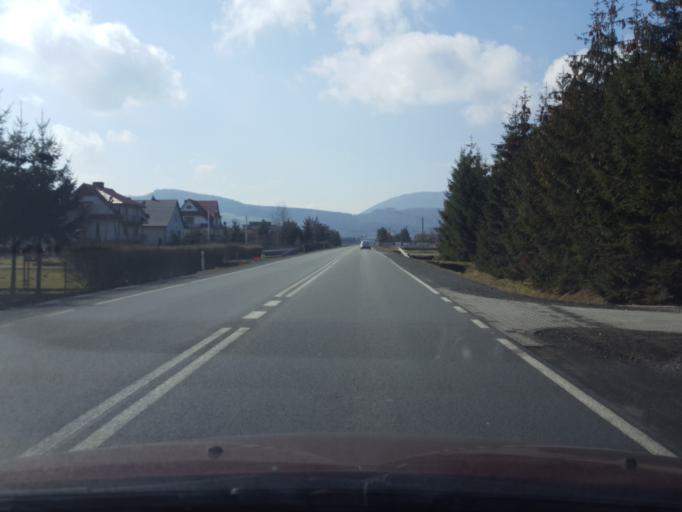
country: PL
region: Lesser Poland Voivodeship
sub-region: Powiat nowosadecki
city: Lososina Dolna
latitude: 49.7526
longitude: 20.6341
